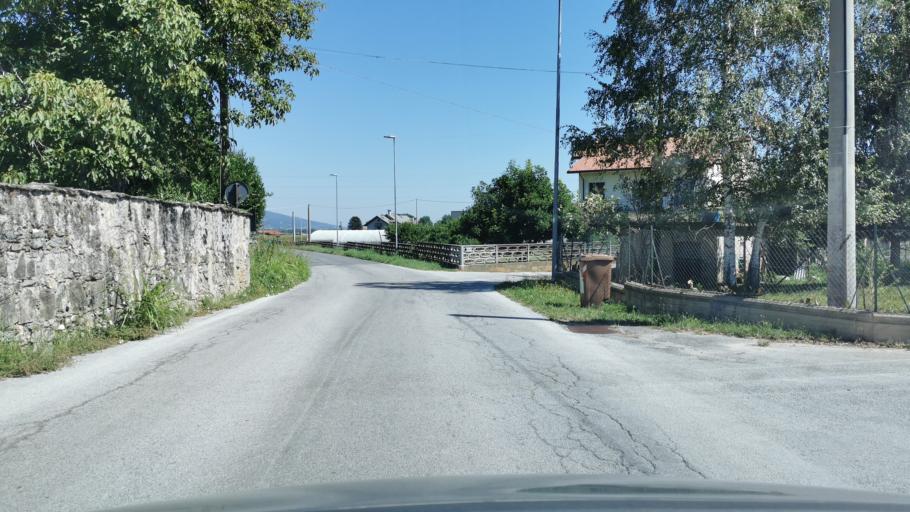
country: IT
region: Piedmont
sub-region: Provincia di Cuneo
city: Caraglio
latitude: 44.4238
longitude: 7.4337
